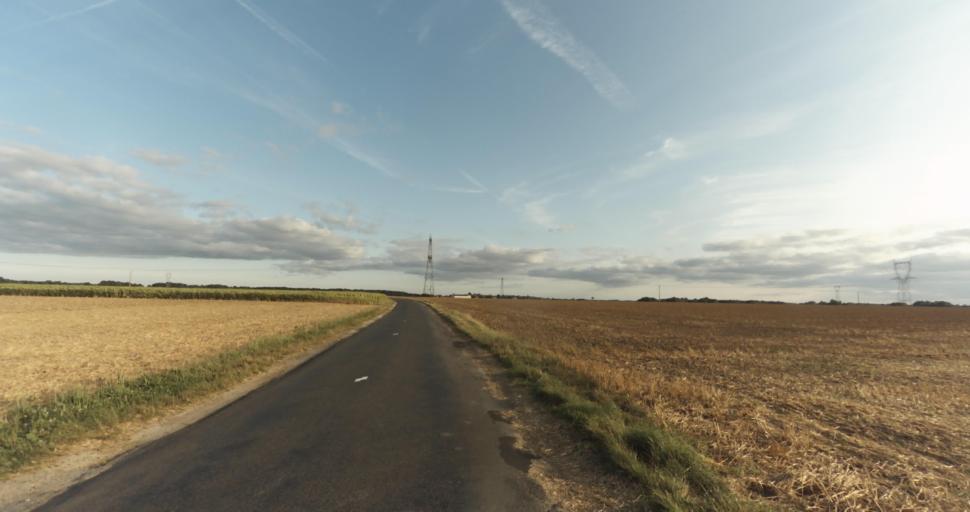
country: FR
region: Haute-Normandie
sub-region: Departement de l'Eure
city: Marcilly-sur-Eure
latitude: 48.8601
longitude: 1.2726
